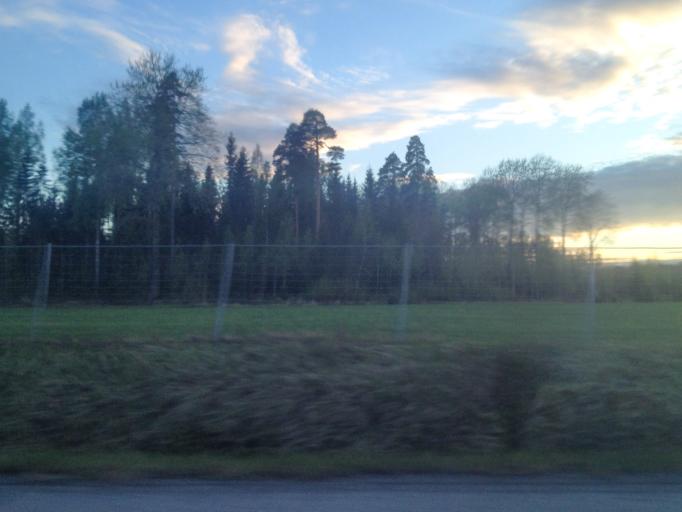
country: FI
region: Uusimaa
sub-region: Helsinki
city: Nurmijaervi
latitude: 60.4770
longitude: 24.8488
